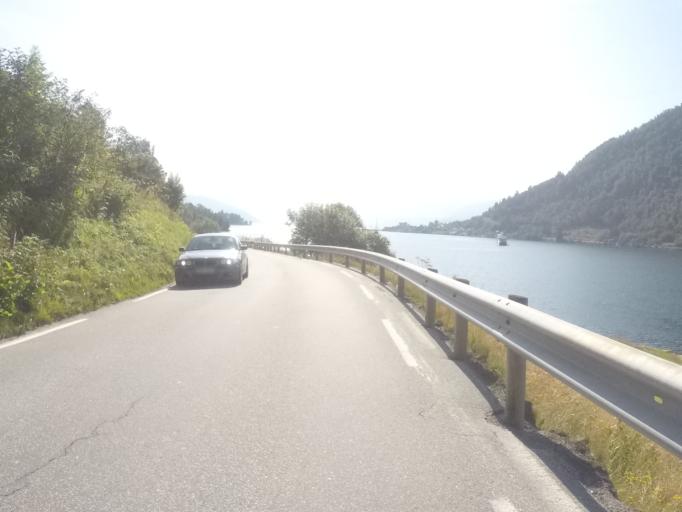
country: NO
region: Sogn og Fjordane
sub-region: Balestrand
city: Balestrand
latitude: 61.2197
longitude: 6.5051
